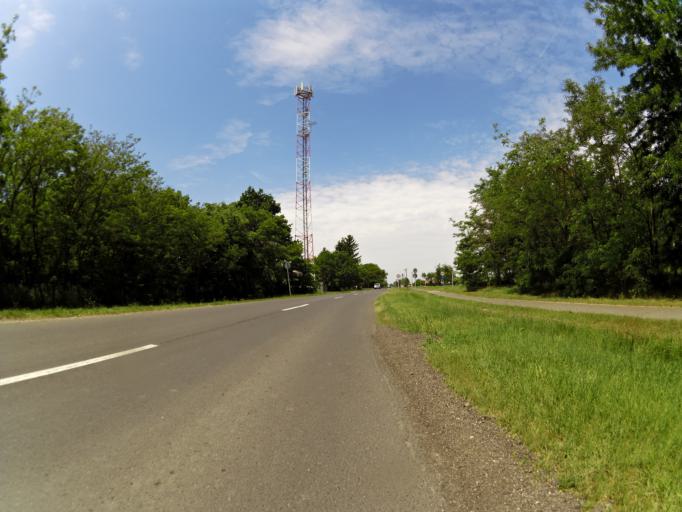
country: HU
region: Csongrad
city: Opusztaszer
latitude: 46.4883
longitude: 20.0756
